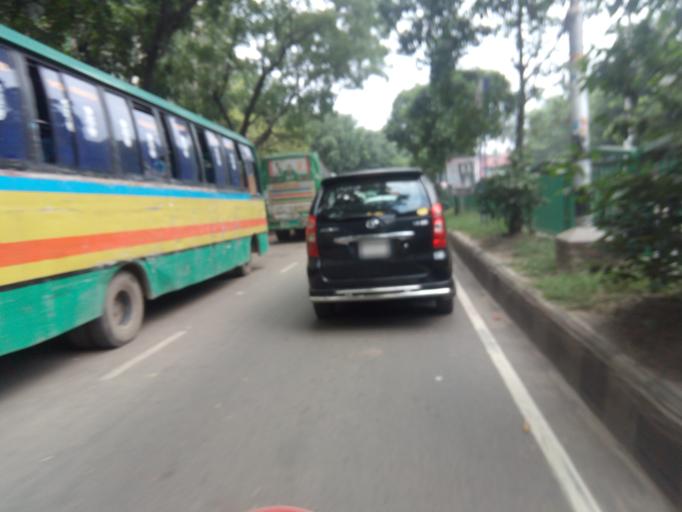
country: BD
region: Dhaka
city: Azimpur
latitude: 23.7254
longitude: 90.3868
